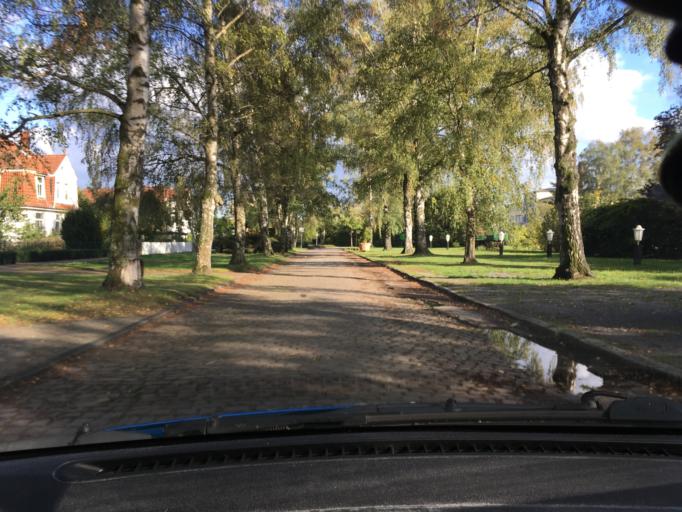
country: DE
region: Lower Saxony
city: Bad Munder am Deister
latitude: 52.1926
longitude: 9.4548
